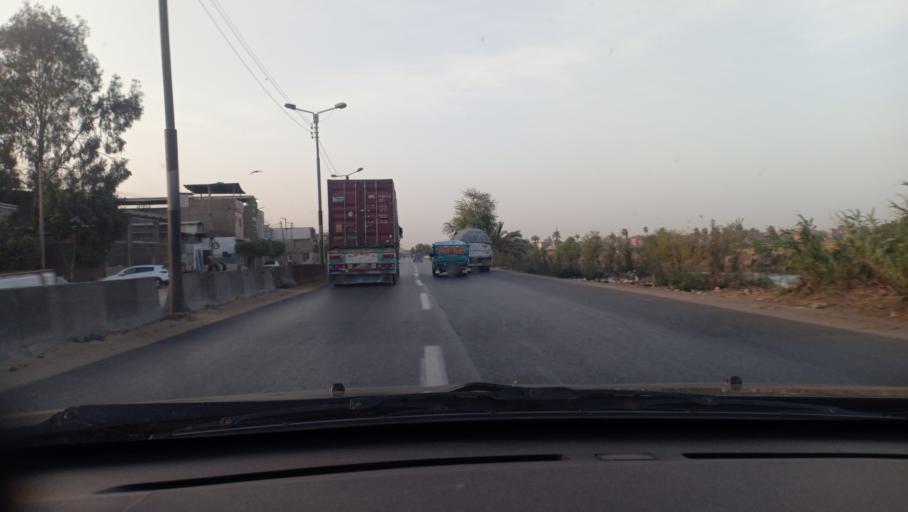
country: EG
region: Muhafazat al Gharbiyah
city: Zifta
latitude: 30.6592
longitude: 31.2845
